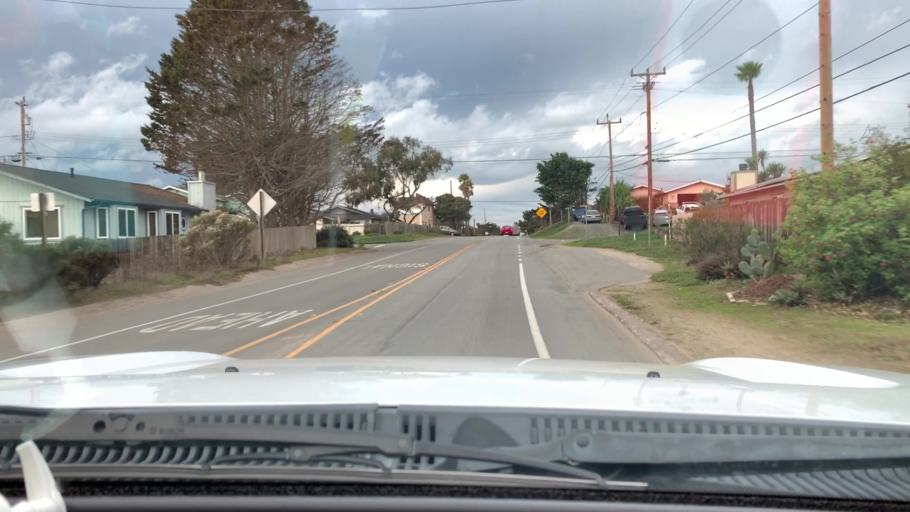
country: US
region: California
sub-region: San Luis Obispo County
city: Los Osos
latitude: 35.3300
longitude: -120.8248
